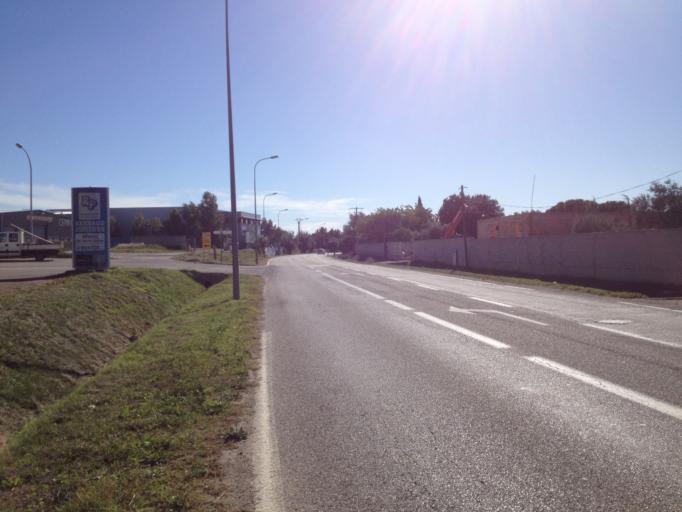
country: FR
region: Provence-Alpes-Cote d'Azur
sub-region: Departement du Vaucluse
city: Bedarrides
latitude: 44.0370
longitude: 4.8893
